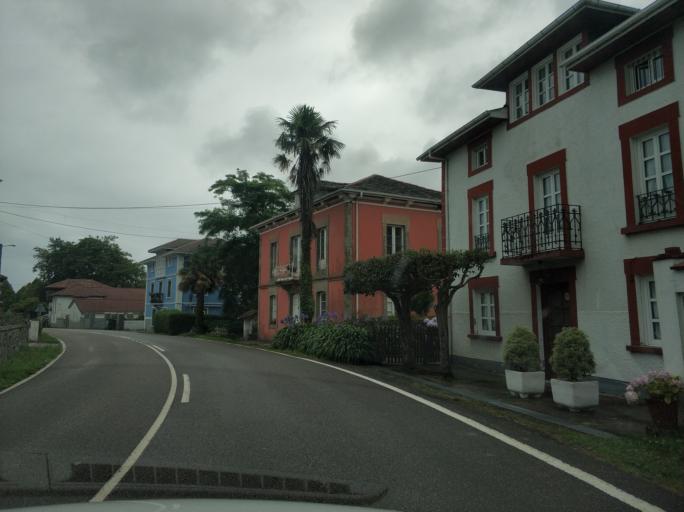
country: ES
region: Asturias
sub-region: Province of Asturias
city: Salas
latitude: 43.5446
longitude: -6.3881
